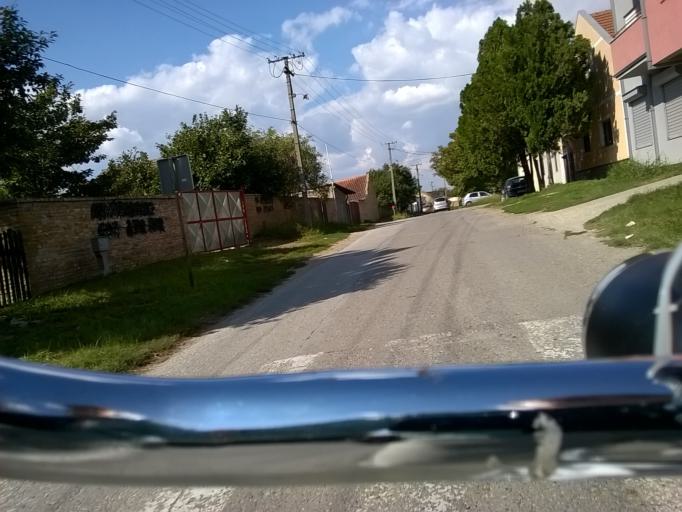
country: RS
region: Autonomna Pokrajina Vojvodina
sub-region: Juznobanatski Okrug
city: Pancevo
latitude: 44.8821
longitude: 20.6322
